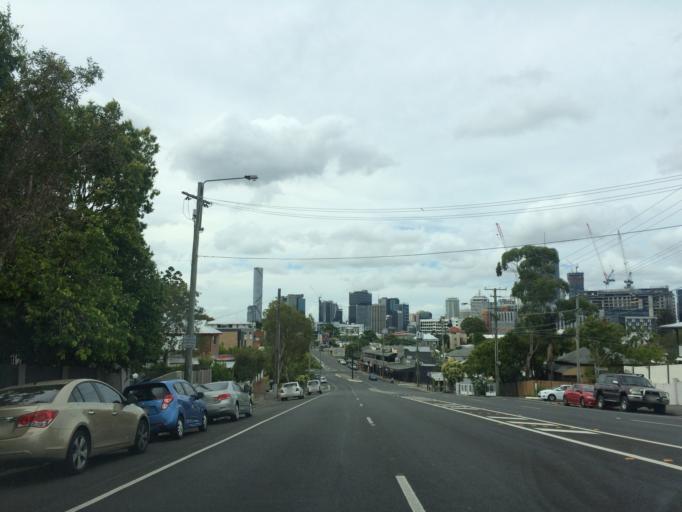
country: AU
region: Queensland
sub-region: Brisbane
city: South Brisbane
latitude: -27.4863
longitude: 153.0194
